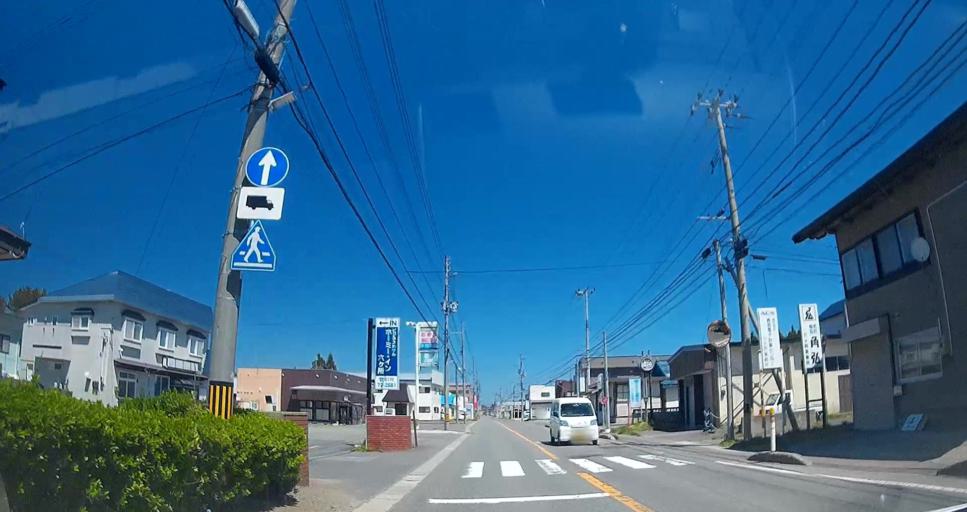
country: JP
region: Aomori
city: Misawa
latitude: 40.9646
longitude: 141.3747
